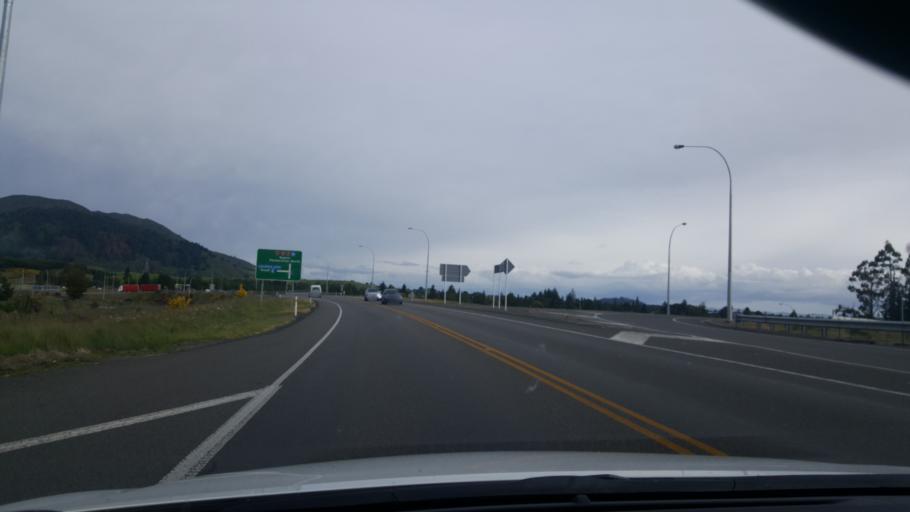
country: NZ
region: Waikato
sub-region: Taupo District
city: Taupo
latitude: -38.6669
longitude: 176.1025
